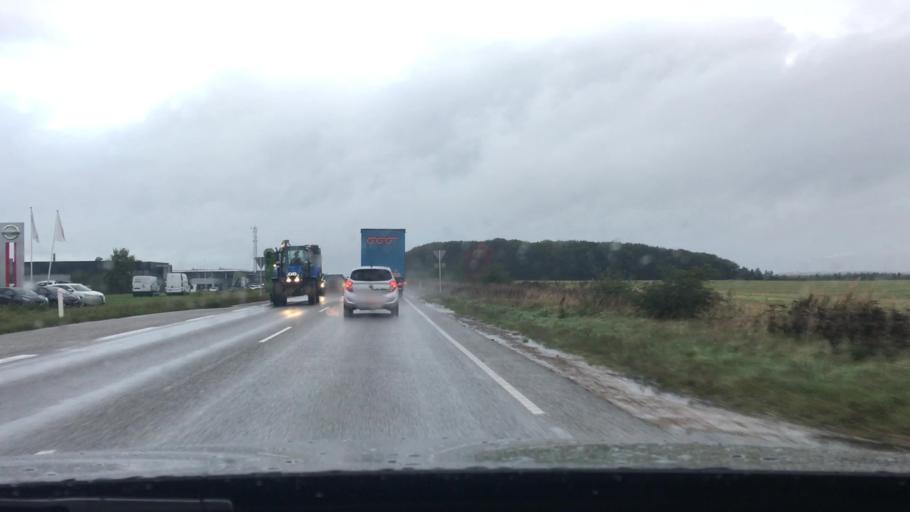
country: DK
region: Central Jutland
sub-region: Holstebro Kommune
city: Holstebro
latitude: 56.3363
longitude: 8.6464
